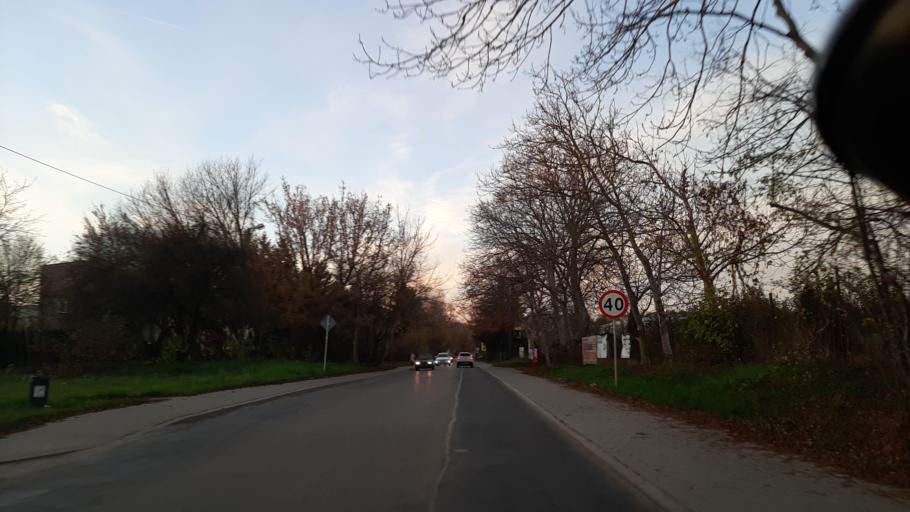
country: PL
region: Lublin Voivodeship
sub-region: Powiat lubelski
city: Lublin
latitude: 51.2739
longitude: 22.5096
